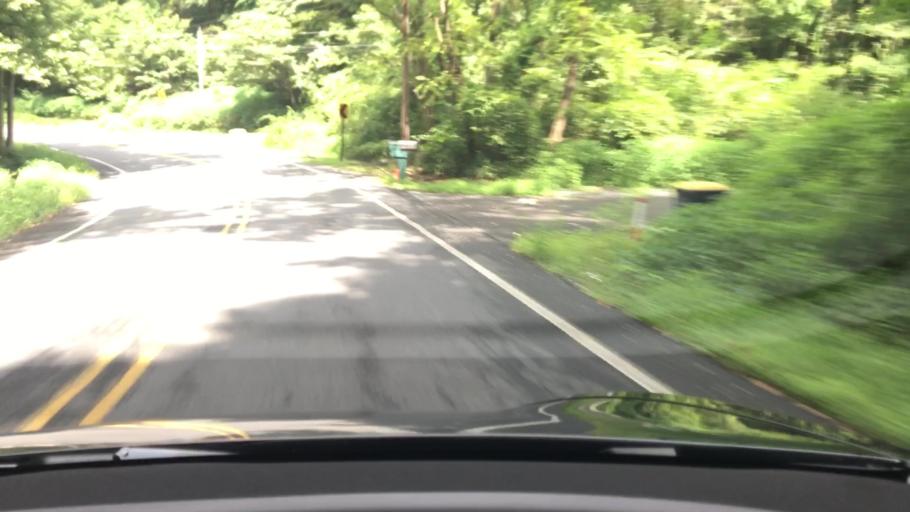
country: US
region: Pennsylvania
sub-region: Cumberland County
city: New Cumberland
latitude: 40.1892
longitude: -76.8721
